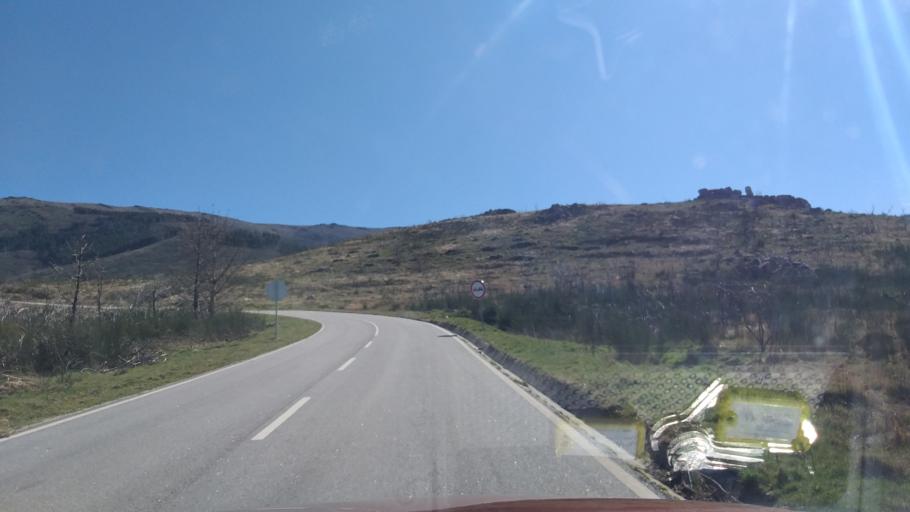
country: PT
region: Guarda
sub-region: Manteigas
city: Manteigas
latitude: 40.4886
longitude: -7.5660
